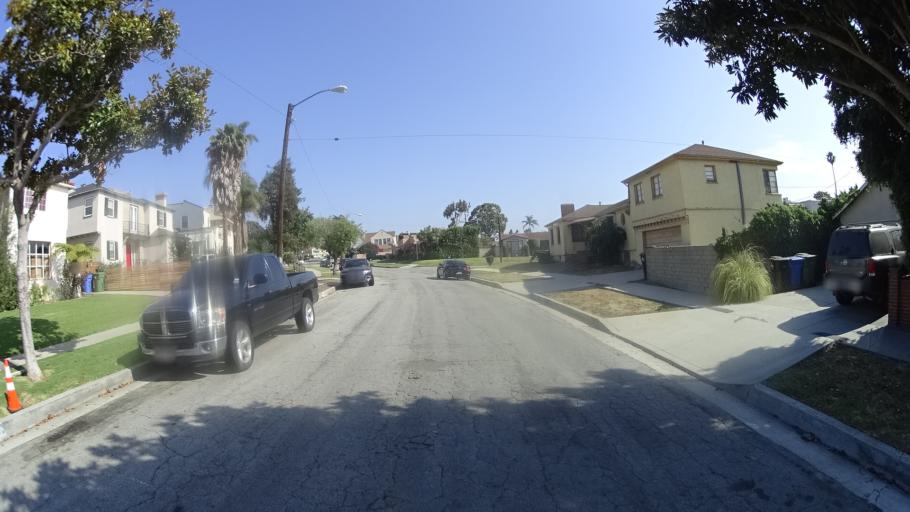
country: US
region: California
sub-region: Los Angeles County
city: View Park-Windsor Hills
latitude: 33.9969
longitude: -118.3346
